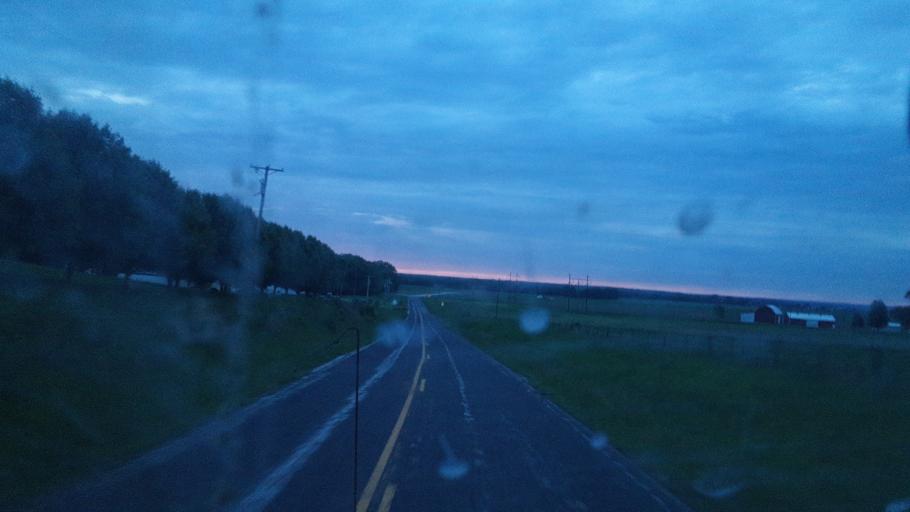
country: US
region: Missouri
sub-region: Clark County
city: Kahoka
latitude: 40.4307
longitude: -91.5792
